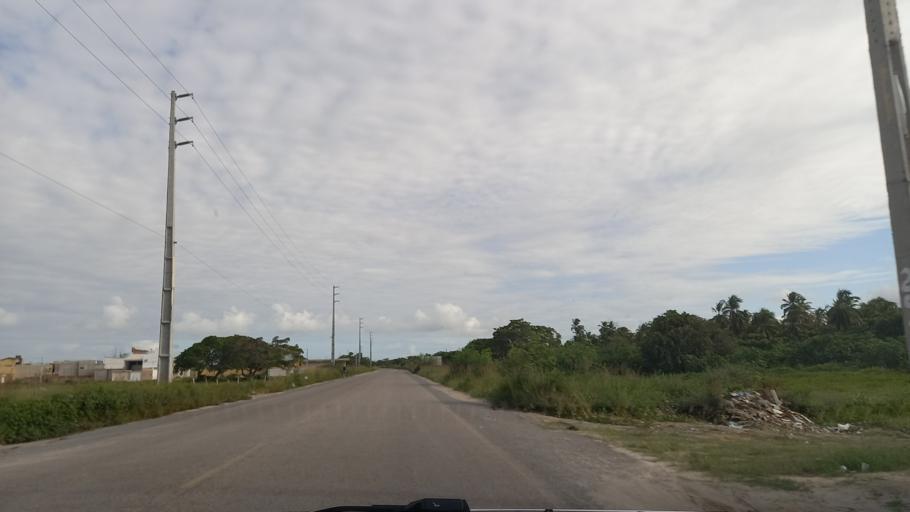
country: BR
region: Pernambuco
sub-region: Tamandare
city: Tamandare
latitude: -8.7323
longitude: -35.0958
